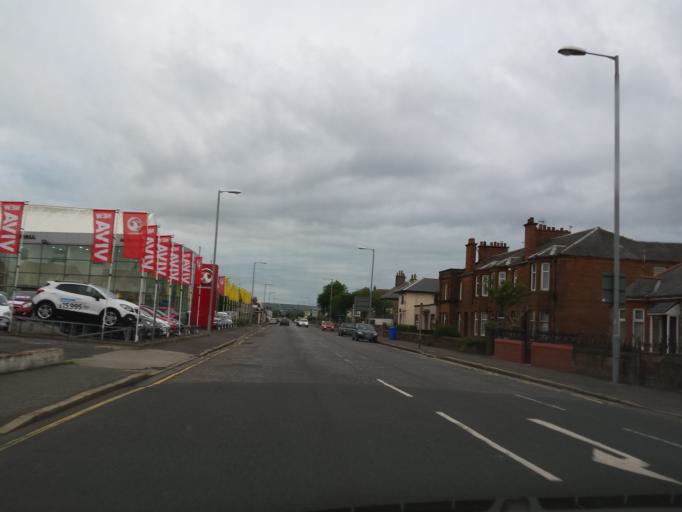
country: GB
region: Scotland
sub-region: South Ayrshire
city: Prestwick
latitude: 55.4830
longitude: -4.6183
